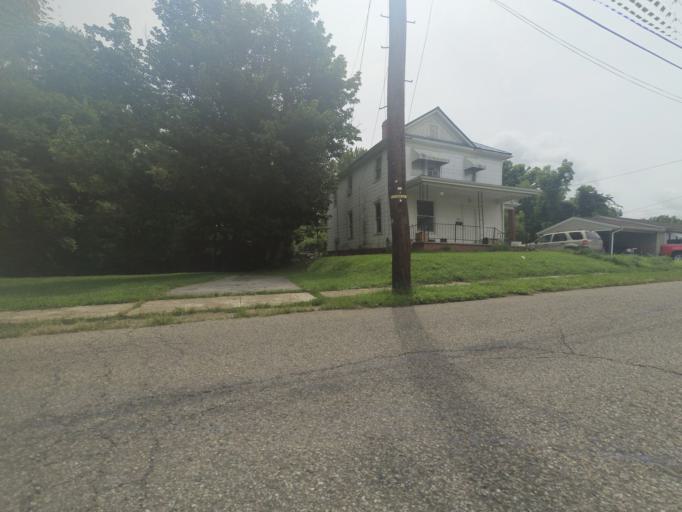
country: US
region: West Virginia
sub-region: Cabell County
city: Huntington
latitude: 38.4122
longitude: -82.4056
